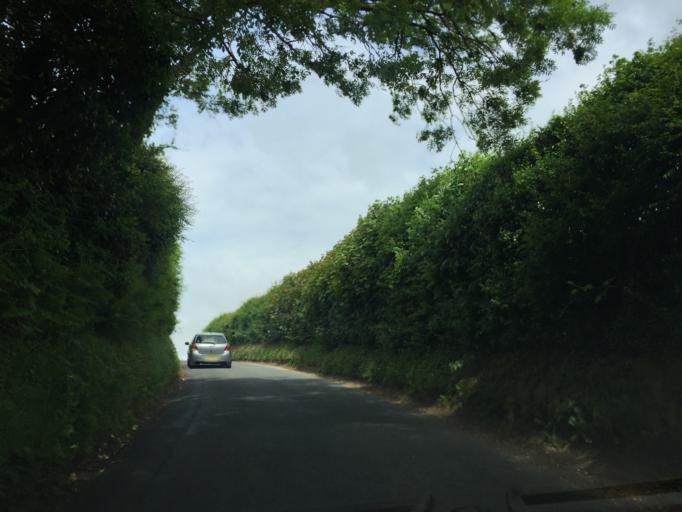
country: GB
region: England
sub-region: Dorset
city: Dorchester
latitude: 50.7206
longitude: -2.3847
